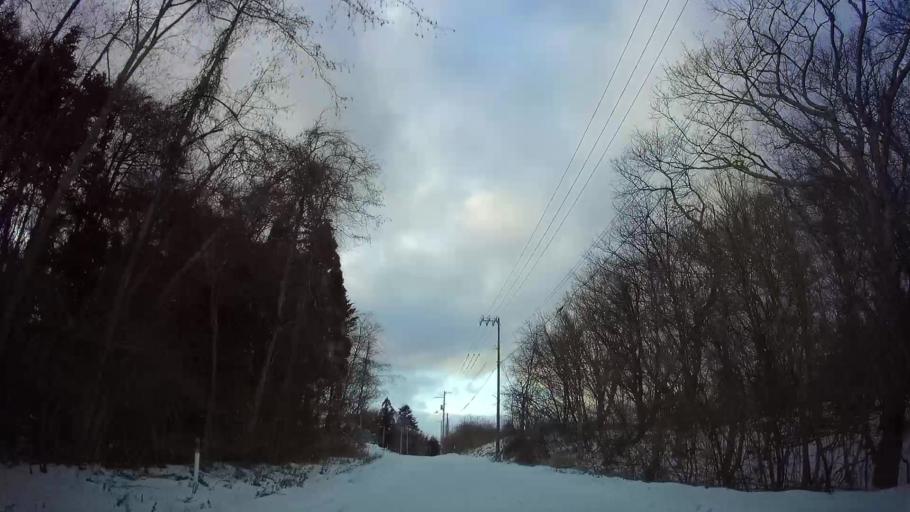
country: JP
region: Hokkaido
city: Nanae
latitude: 42.0201
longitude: 140.8406
